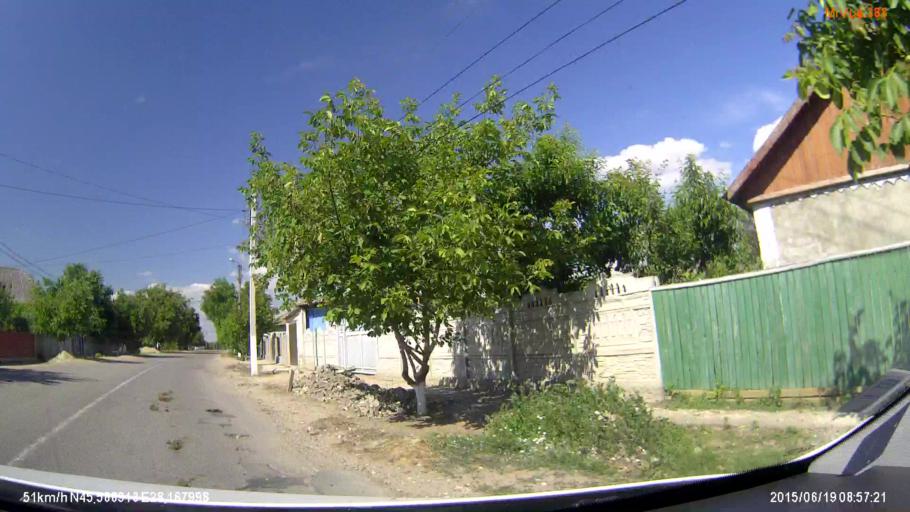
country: MD
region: Cahul
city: Giurgiulesti
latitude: 45.5888
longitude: 28.1680
